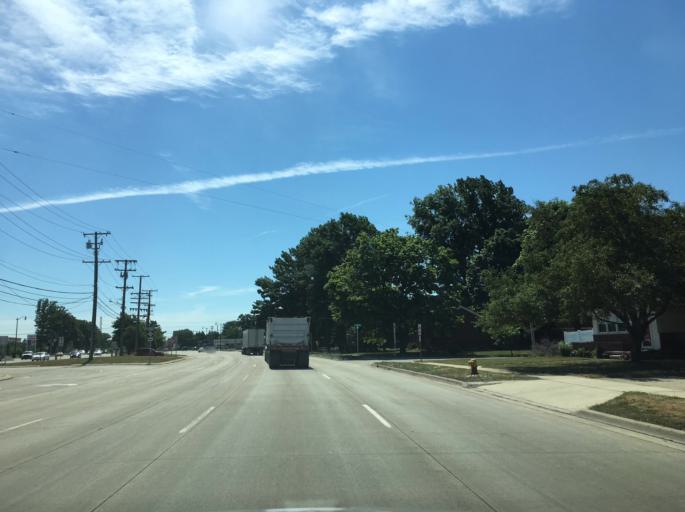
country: US
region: Michigan
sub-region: Wayne County
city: Allen Park
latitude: 42.2632
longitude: -83.2197
